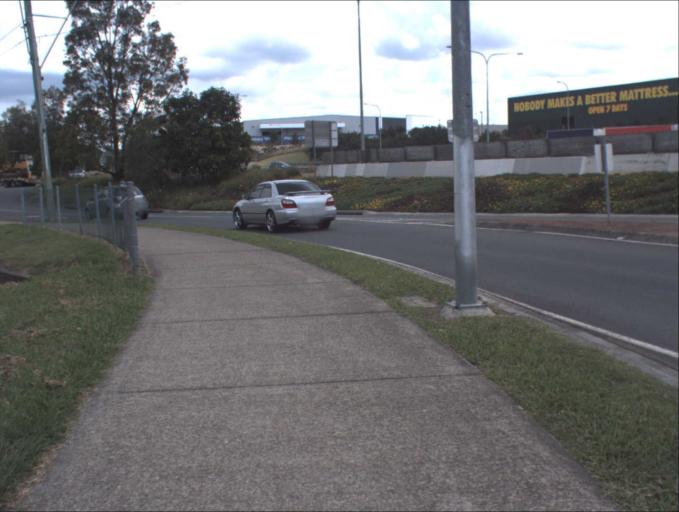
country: AU
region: Queensland
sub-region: Brisbane
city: Sunnybank Hills
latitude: -27.6570
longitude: 153.0395
